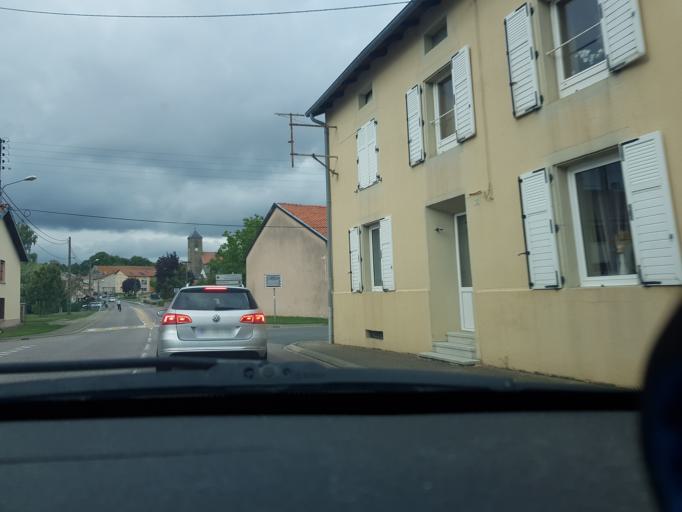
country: FR
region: Lorraine
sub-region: Departement de la Moselle
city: Morhange
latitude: 48.9653
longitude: 6.6119
